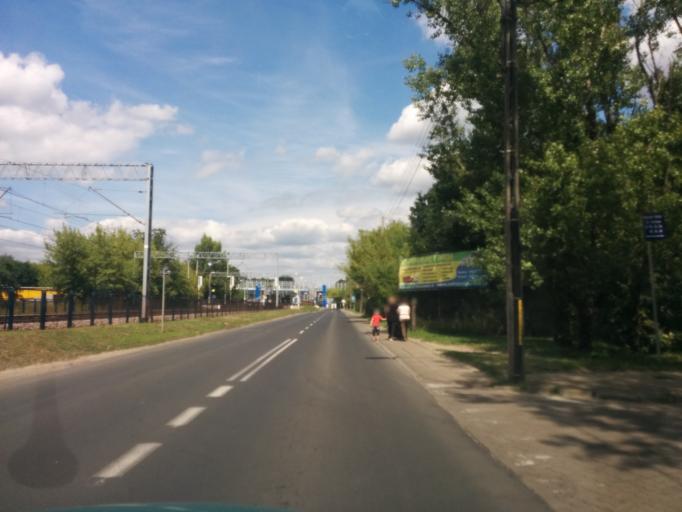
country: PL
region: Masovian Voivodeship
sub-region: Warszawa
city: Bialoleka
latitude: 52.3320
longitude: 20.9873
